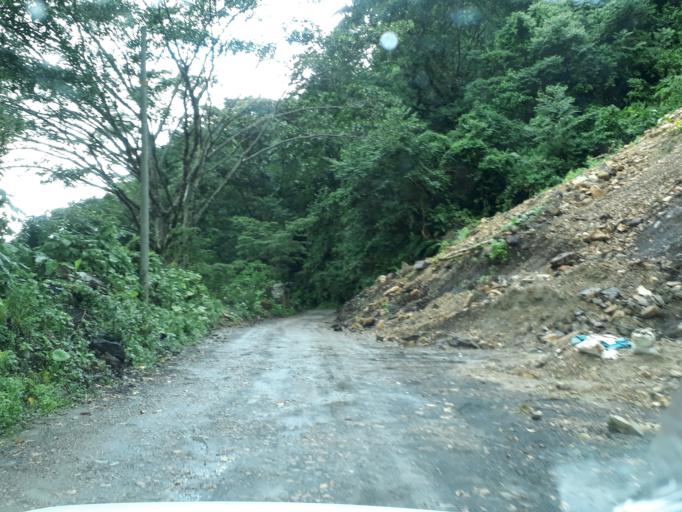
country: CO
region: Cundinamarca
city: Medina
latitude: 4.5854
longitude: -73.3819
